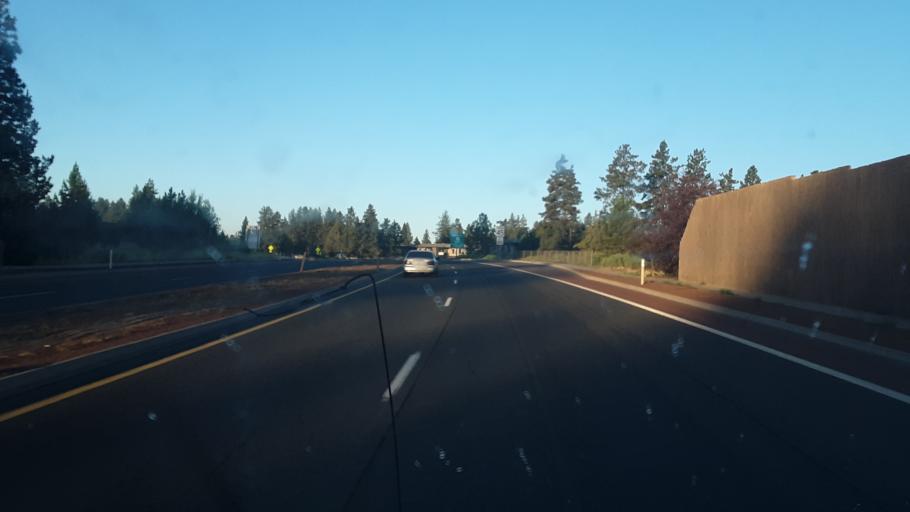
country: US
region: Oregon
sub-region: Deschutes County
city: Bend
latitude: 44.0360
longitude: -121.3121
